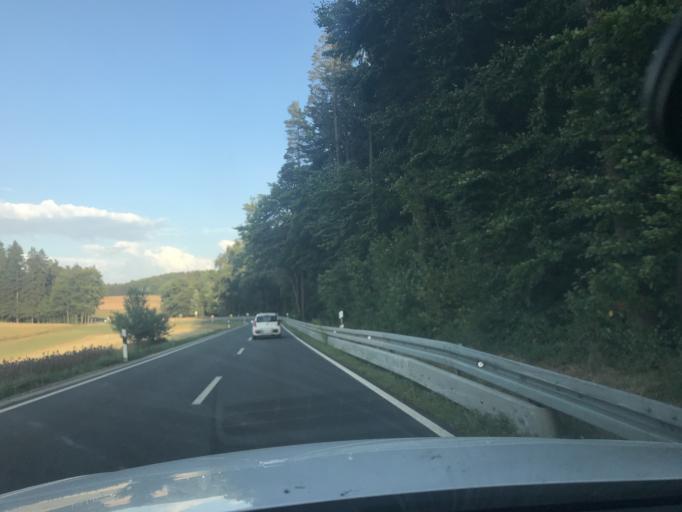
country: DE
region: Bavaria
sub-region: Upper Franconia
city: Obertrubach
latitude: 49.6895
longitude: 11.3733
